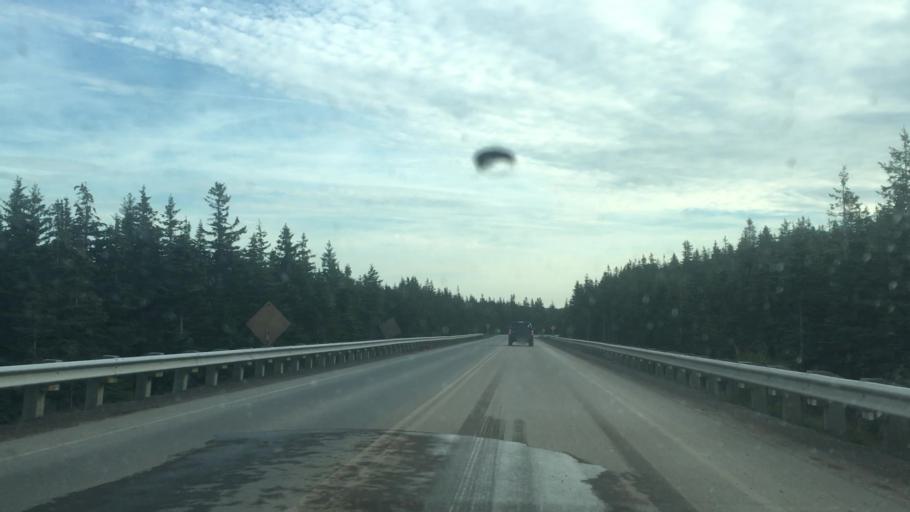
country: CA
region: Nova Scotia
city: Sydney Mines
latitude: 46.8019
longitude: -60.8439
